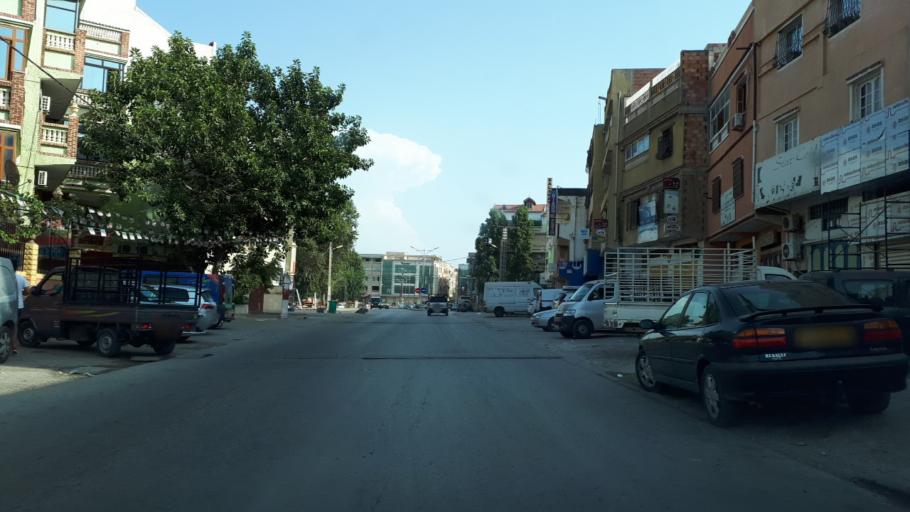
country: DZ
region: Alger
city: Dar el Beida
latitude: 36.7324
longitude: 3.2354
